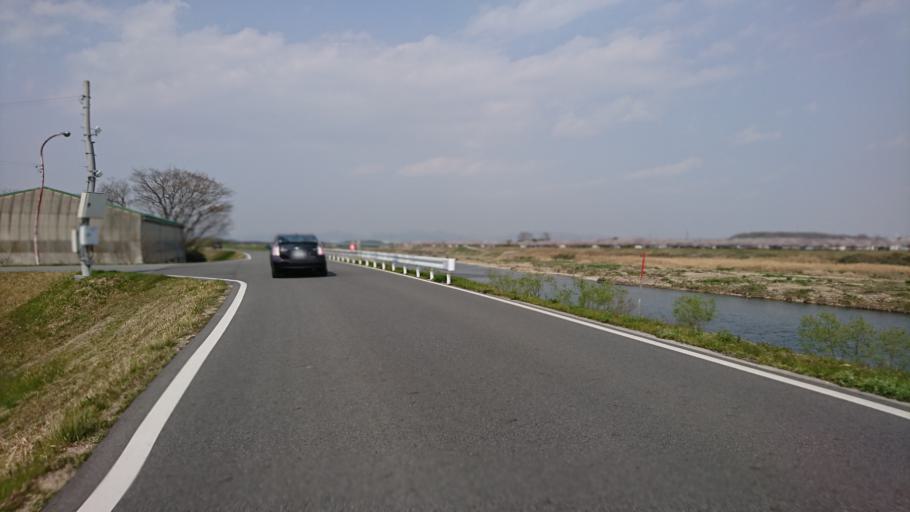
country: JP
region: Hyogo
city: Ono
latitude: 34.8703
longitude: 134.9224
